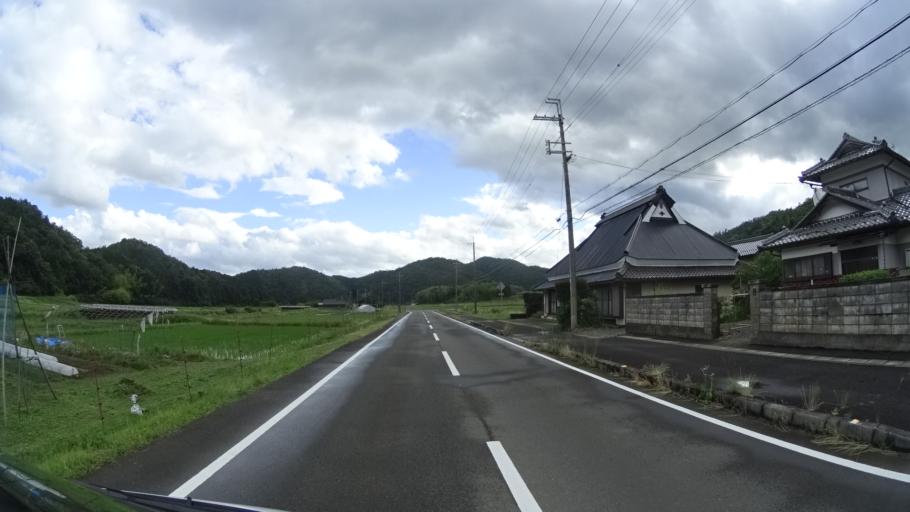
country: JP
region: Kyoto
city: Ayabe
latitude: 35.3818
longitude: 135.2395
